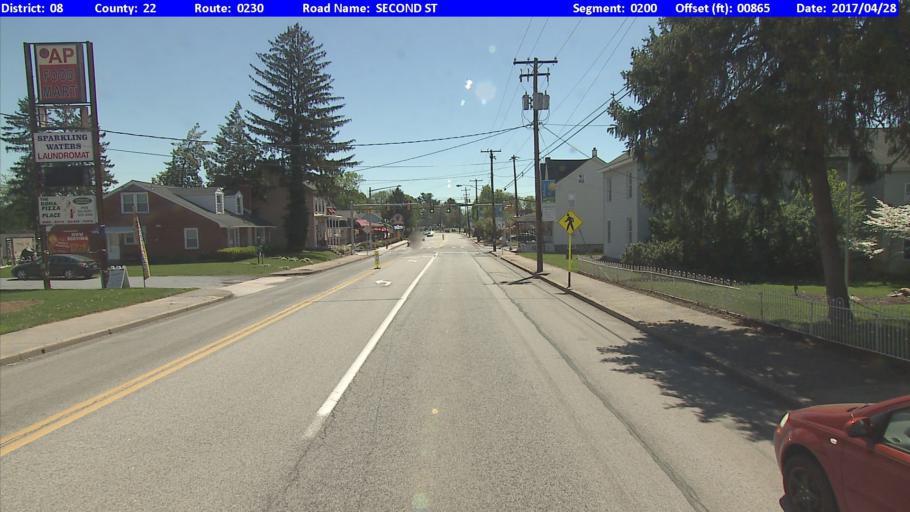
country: US
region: Pennsylvania
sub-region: Dauphin County
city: Highspire
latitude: 40.2084
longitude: -76.7891
